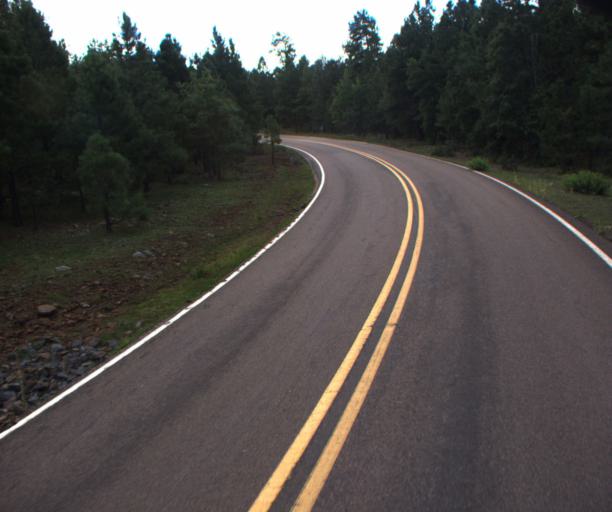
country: US
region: Arizona
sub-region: Navajo County
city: Pinetop-Lakeside
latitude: 34.0227
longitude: -109.7879
